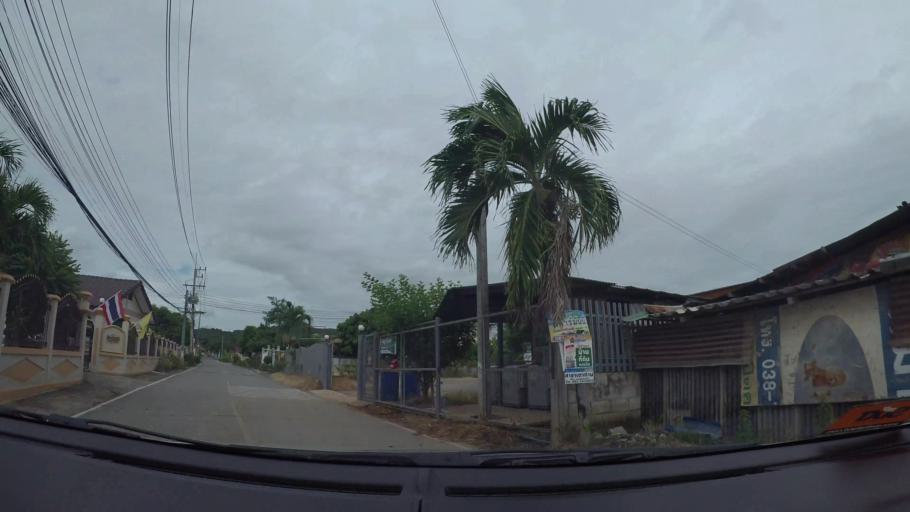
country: TH
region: Chon Buri
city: Sattahip
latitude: 12.7069
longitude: 100.8924
